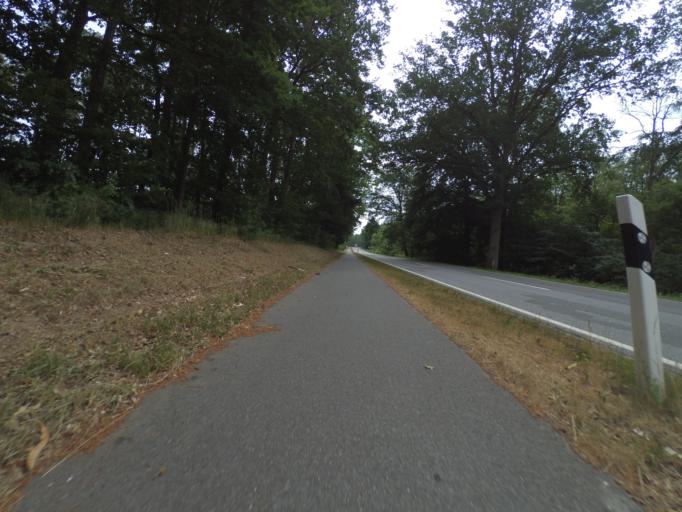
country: DE
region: Mecklenburg-Vorpommern
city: Krakow am See
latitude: 53.6207
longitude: 12.3401
